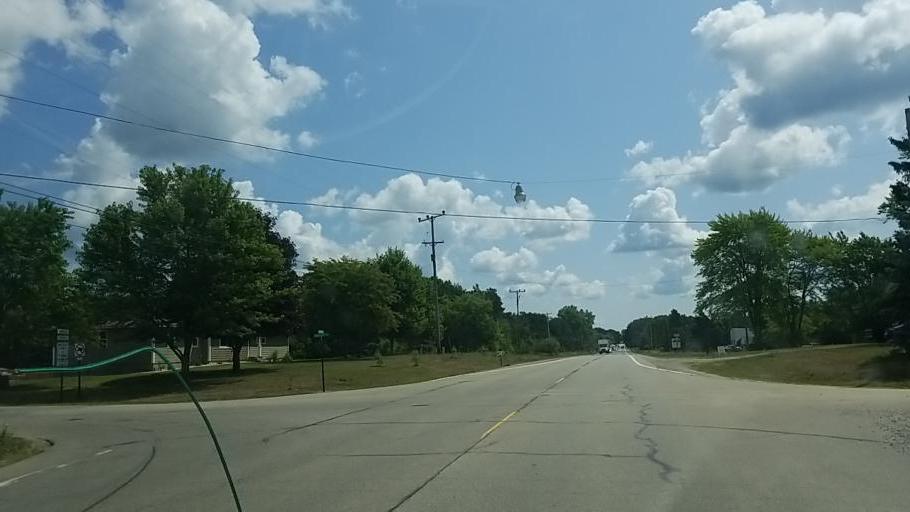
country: US
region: Michigan
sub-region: Muskegon County
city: Ravenna
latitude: 43.2351
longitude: -85.9682
